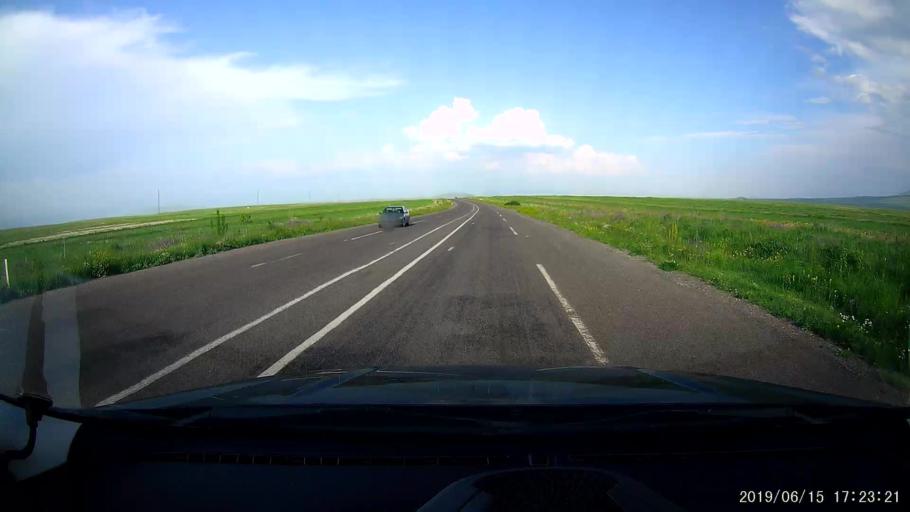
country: TR
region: Kars
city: Basgedikler
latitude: 40.6170
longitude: 43.3611
